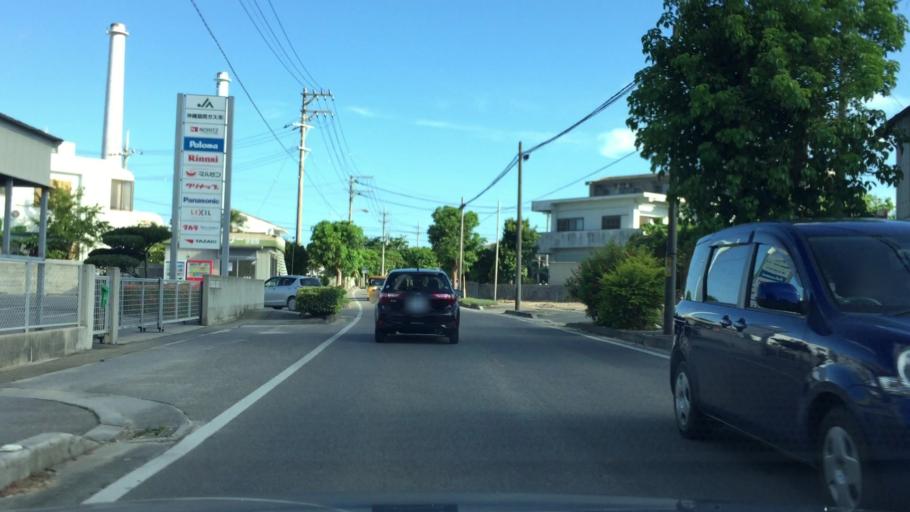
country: JP
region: Okinawa
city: Ishigaki
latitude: 24.3504
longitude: 124.1585
